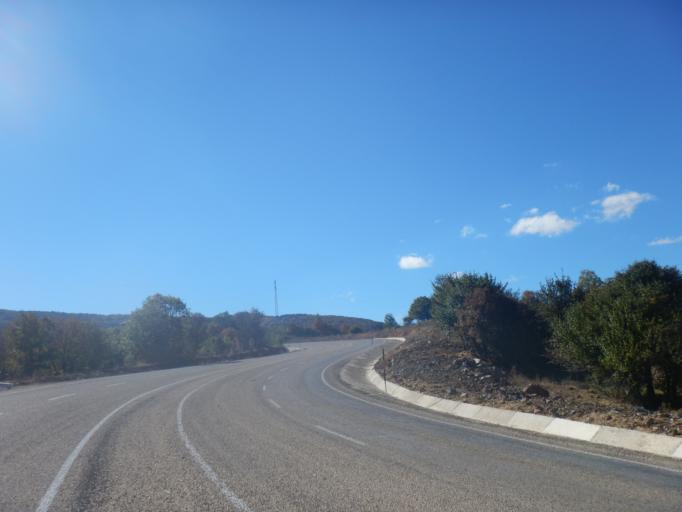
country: TR
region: Ordu
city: Mesudiye
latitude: 40.4422
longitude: 37.7767
